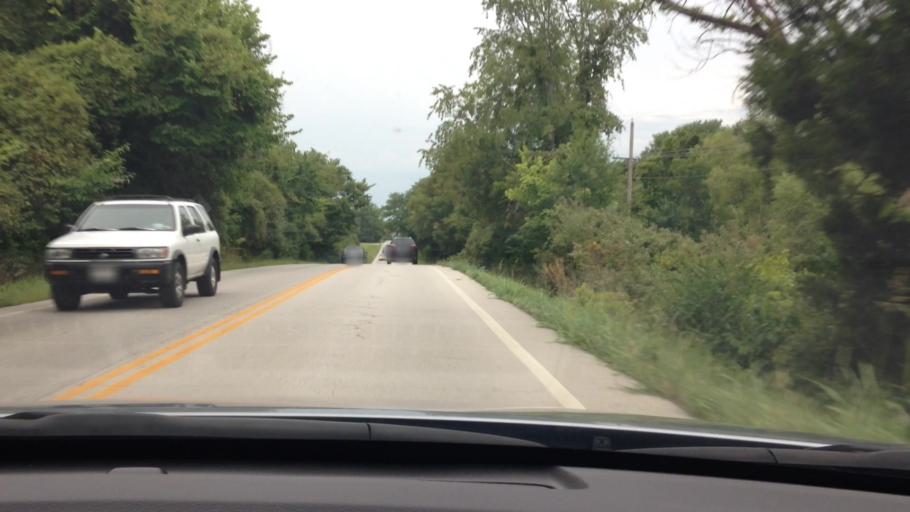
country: US
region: Missouri
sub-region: Platte County
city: Weatherby Lake
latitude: 39.2328
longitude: -94.7849
